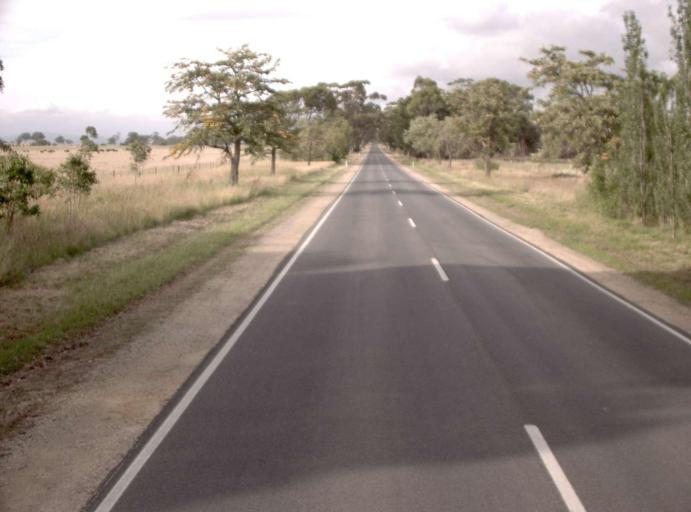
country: AU
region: Victoria
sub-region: Wellington
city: Sale
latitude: -37.9388
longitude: 146.9902
